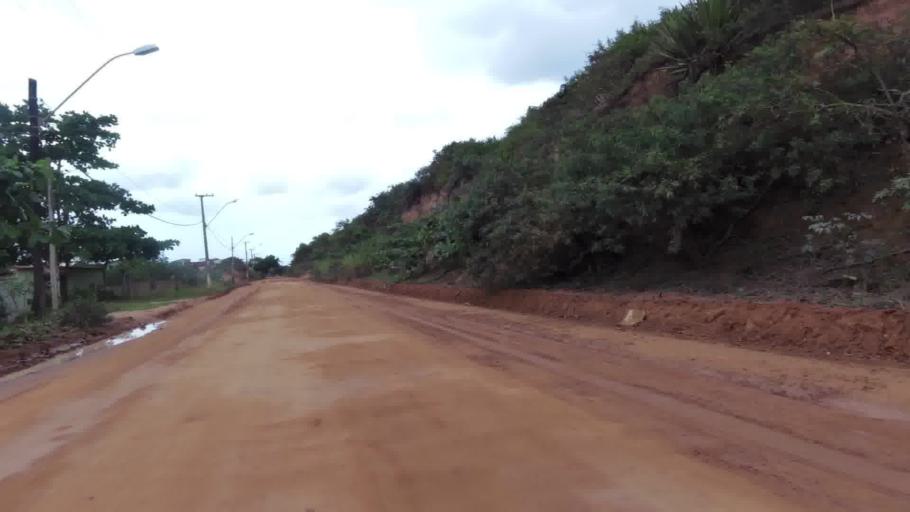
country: BR
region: Espirito Santo
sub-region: Marataizes
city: Marataizes
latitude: -21.0622
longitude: -40.8371
